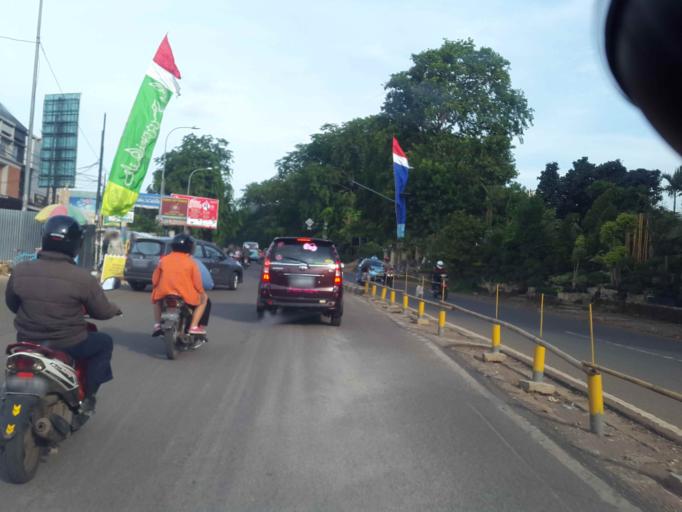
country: ID
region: West Java
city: Bekasi
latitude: -6.2495
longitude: 106.9566
